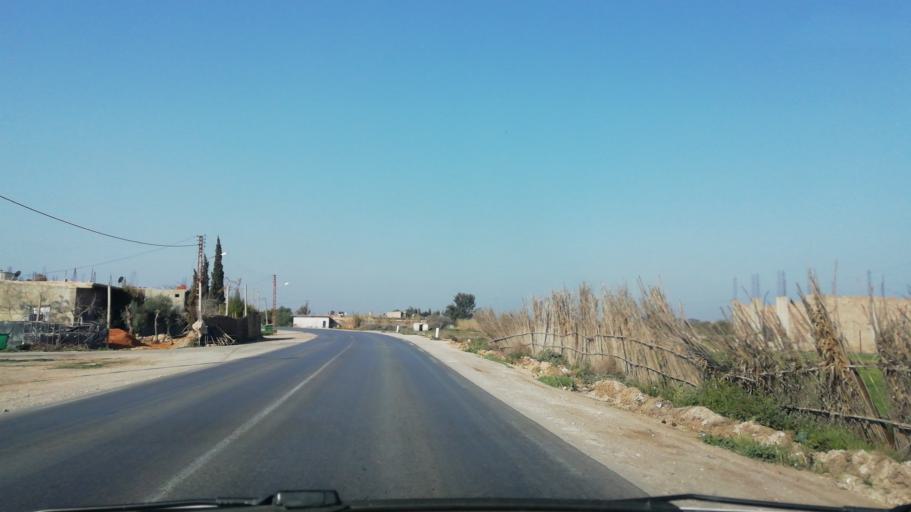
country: DZ
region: Mostaganem
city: Mostaganem
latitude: 35.7591
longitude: 0.0627
